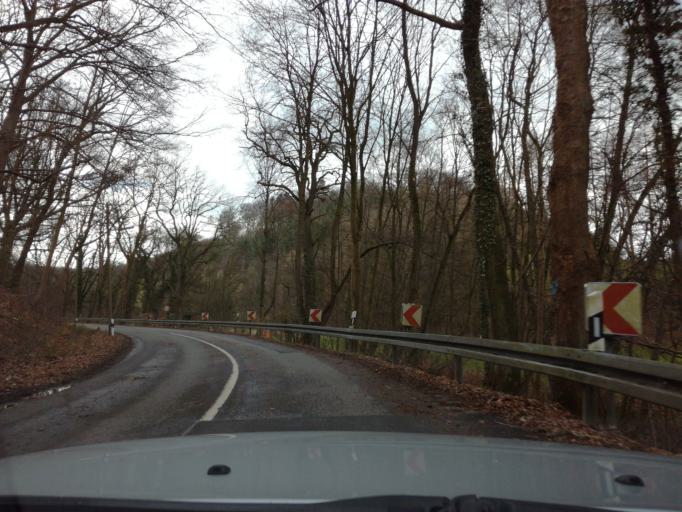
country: DE
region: North Rhine-Westphalia
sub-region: Regierungsbezirk Dusseldorf
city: Velbert
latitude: 51.3735
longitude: 7.0388
